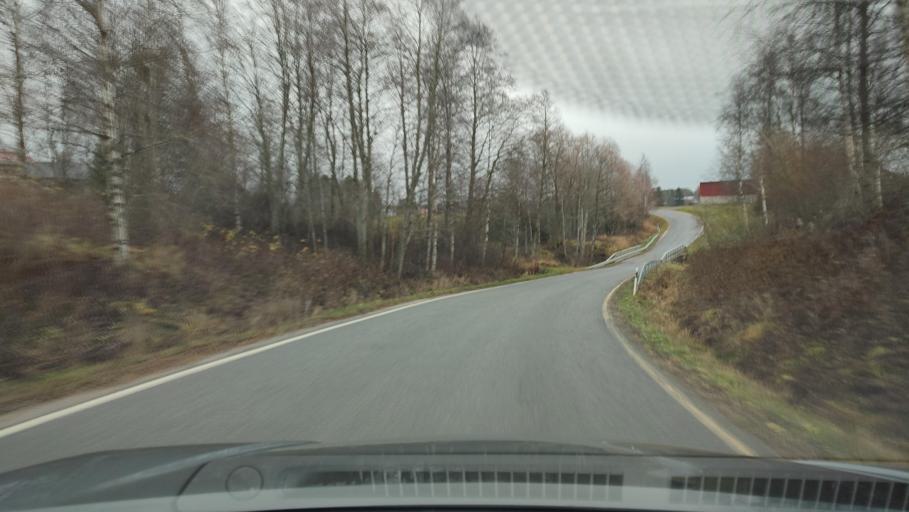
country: FI
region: Southern Ostrobothnia
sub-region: Suupohja
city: Isojoki
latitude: 62.1922
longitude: 21.9648
